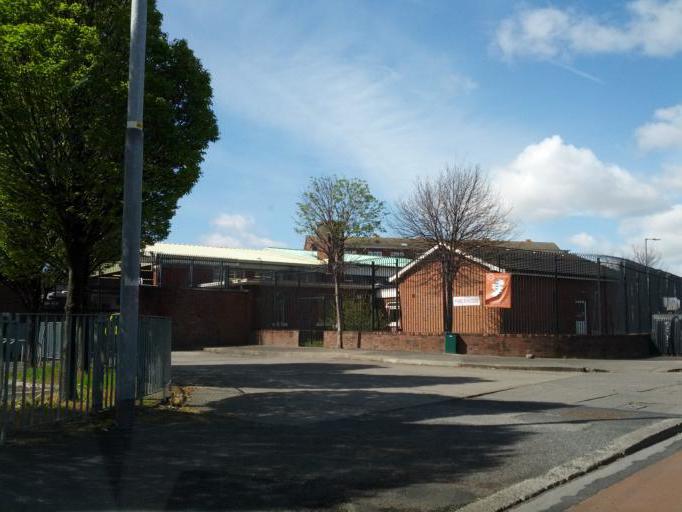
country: IE
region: Leinster
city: Rialto
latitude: 53.3316
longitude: -6.2920
